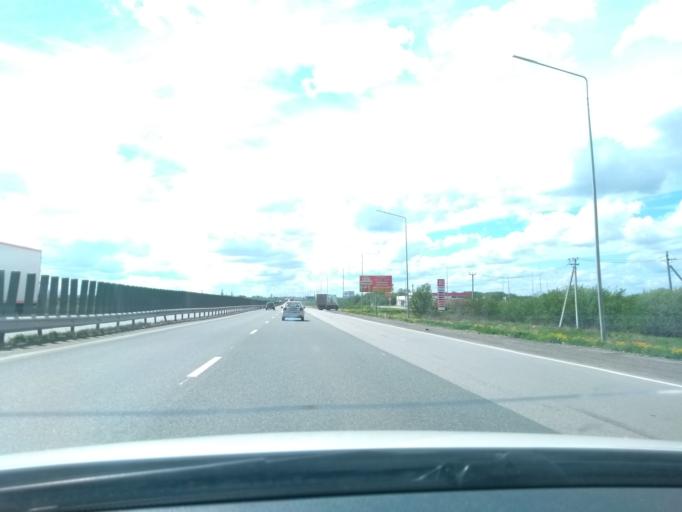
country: RU
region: Perm
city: Froly
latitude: 57.9329
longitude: 56.2057
